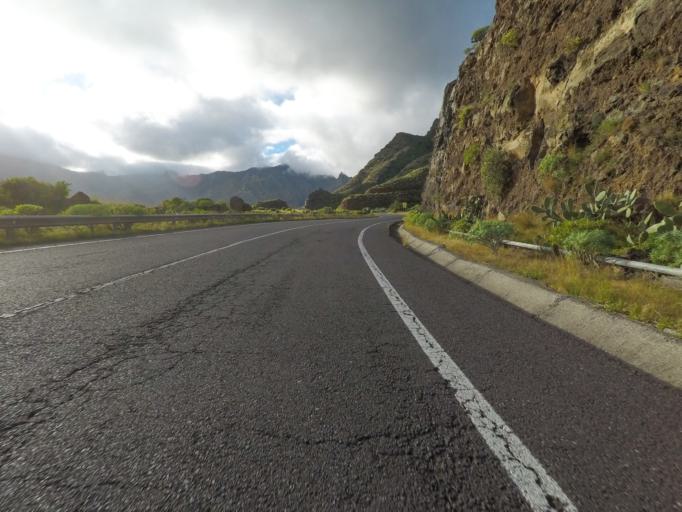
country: ES
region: Canary Islands
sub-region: Provincia de Santa Cruz de Tenerife
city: San Sebastian de la Gomera
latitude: 28.1232
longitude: -17.1559
